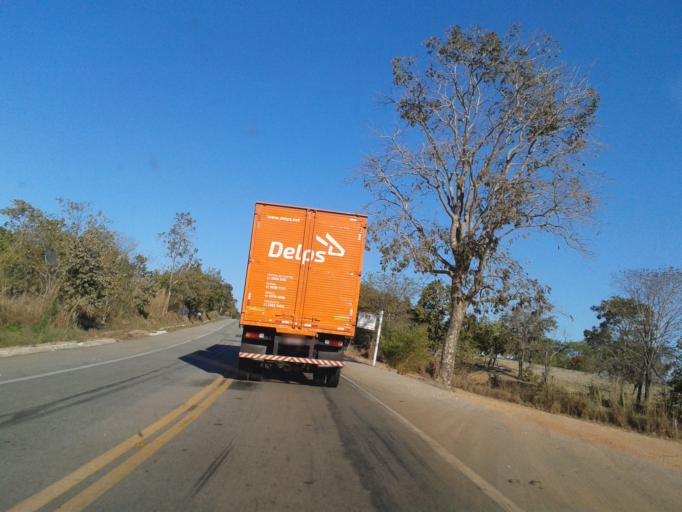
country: BR
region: Goias
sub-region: Itapirapua
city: Itapirapua
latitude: -15.3154
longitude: -50.4422
